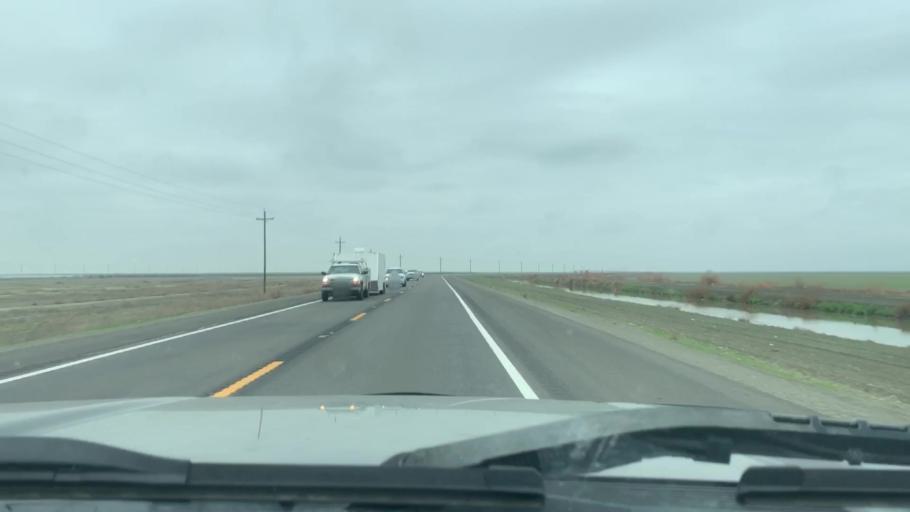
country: US
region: California
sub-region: Kings County
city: Kettleman City
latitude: 36.0568
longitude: -119.9415
